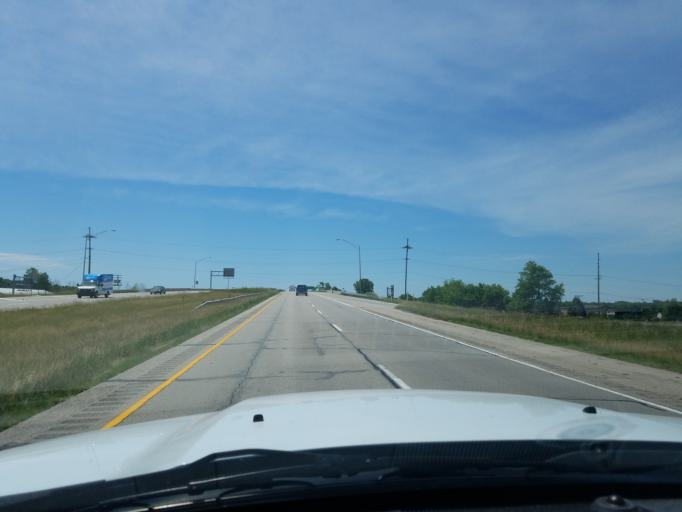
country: US
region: Indiana
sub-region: Delaware County
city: Muncie
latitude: 40.1942
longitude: -85.3364
